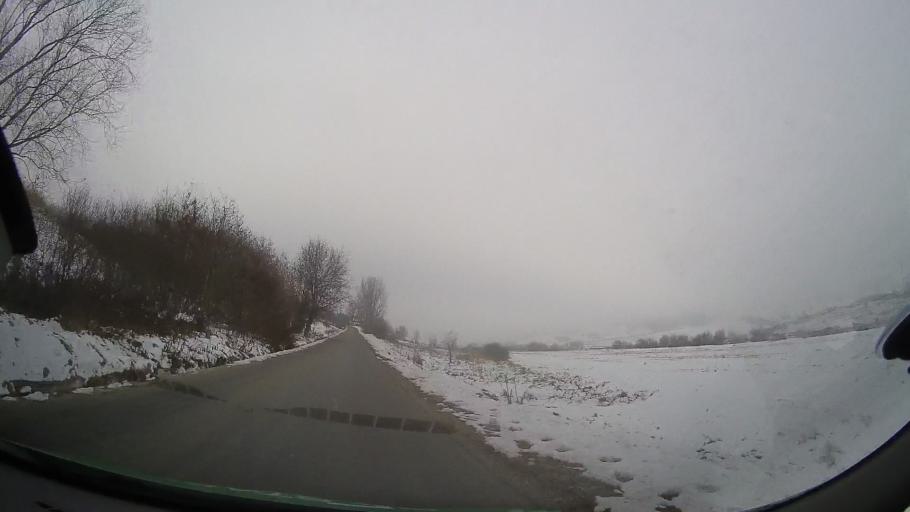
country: RO
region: Bacau
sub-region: Comuna Vultureni
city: Vultureni
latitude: 46.3086
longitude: 27.2927
